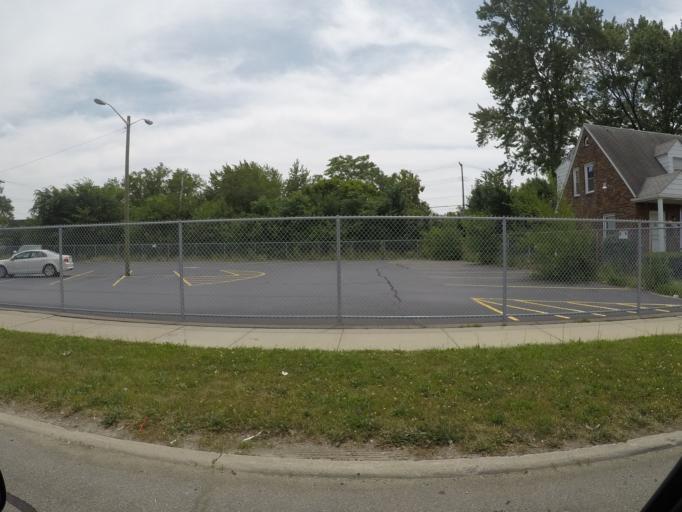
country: US
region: Michigan
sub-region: Macomb County
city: Eastpointe
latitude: 42.4355
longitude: -82.9576
